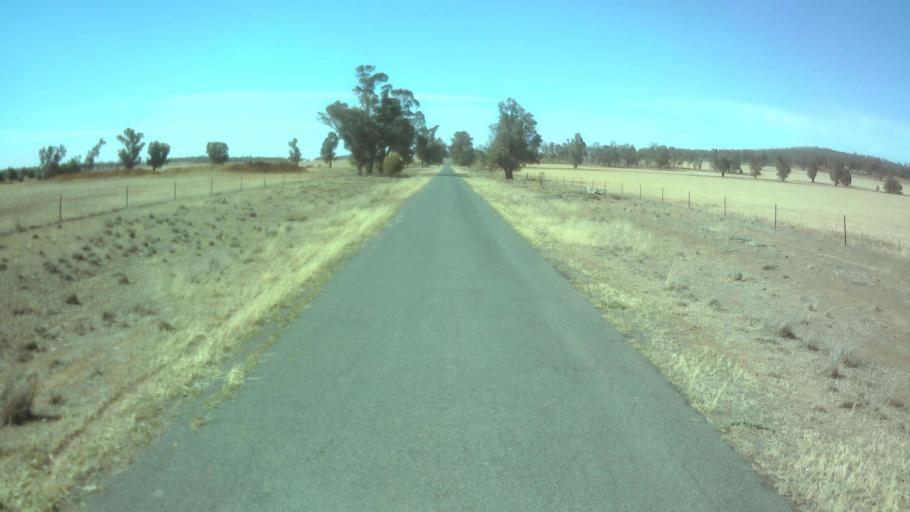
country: AU
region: New South Wales
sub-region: Forbes
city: Forbes
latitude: -33.7382
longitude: 147.7413
